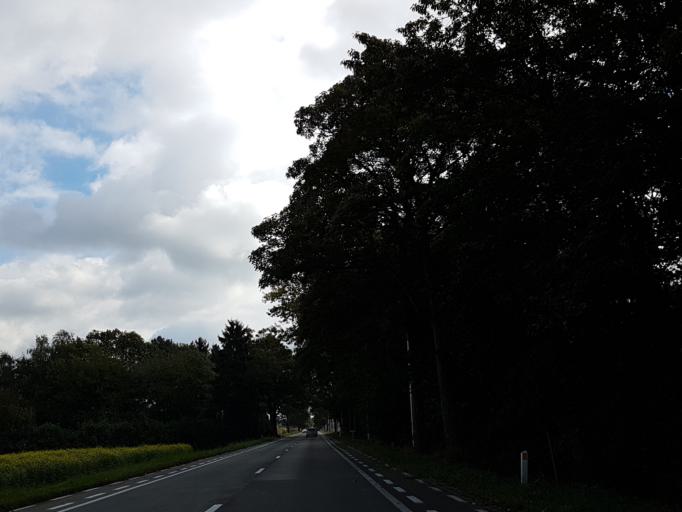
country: BE
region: Flanders
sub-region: Provincie Vlaams-Brabant
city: Boutersem
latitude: 50.8527
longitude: 4.8036
